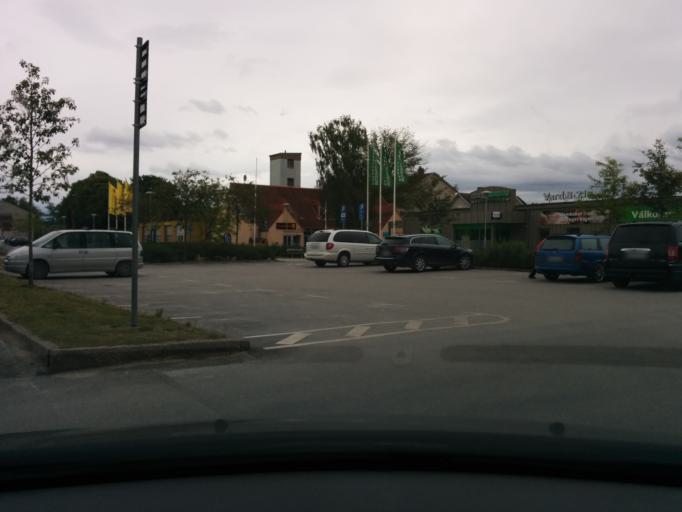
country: SE
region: Gotland
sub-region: Gotland
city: Slite
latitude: 57.7045
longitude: 18.8024
